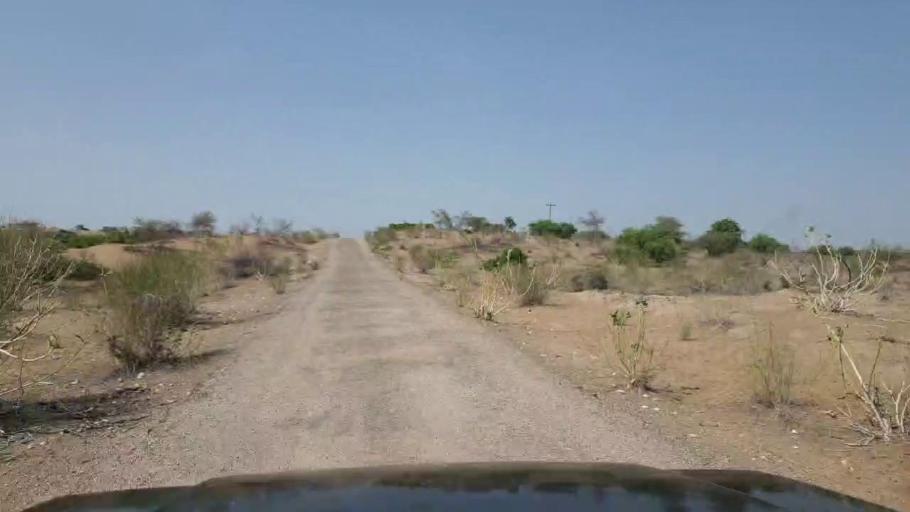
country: PK
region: Sindh
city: Mithi
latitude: 24.9740
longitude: 69.9714
